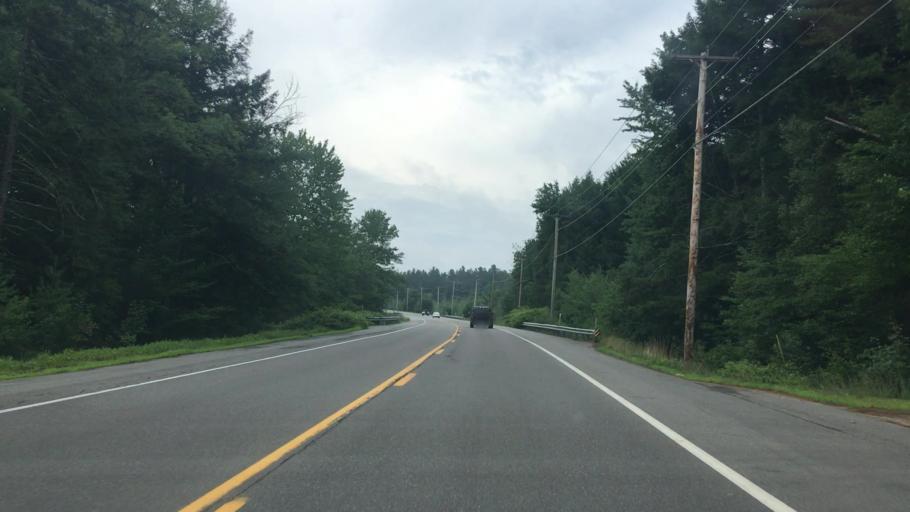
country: US
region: Maine
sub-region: York County
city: Lebanon
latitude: 43.4014
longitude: -70.8752
